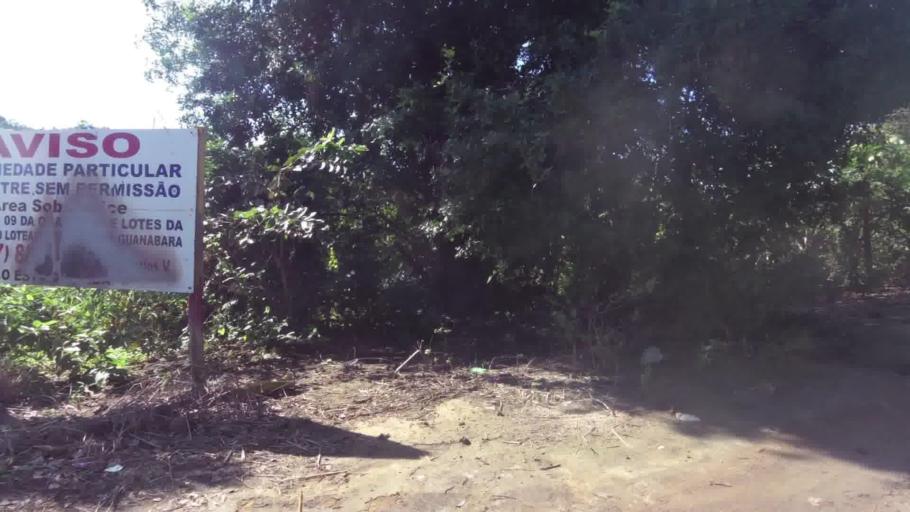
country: BR
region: Espirito Santo
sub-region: Piuma
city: Piuma
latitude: -20.8187
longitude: -40.6177
